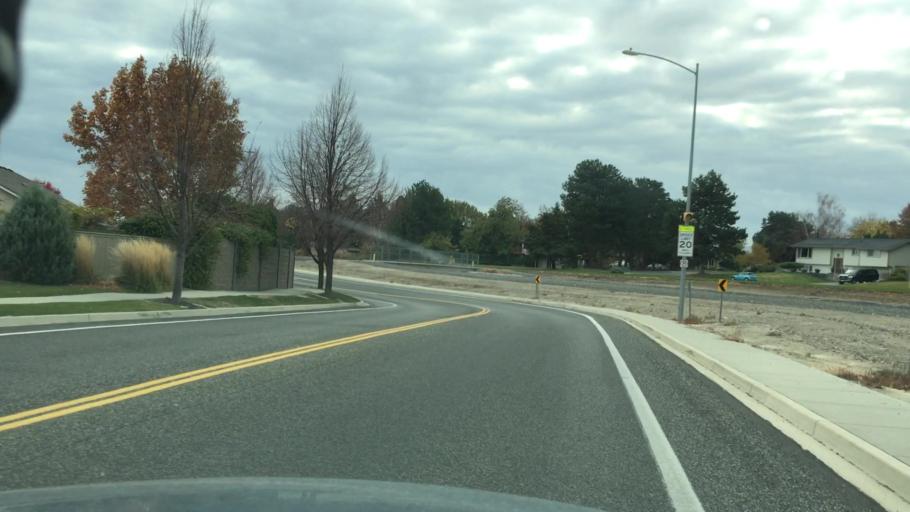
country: US
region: Washington
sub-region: Franklin County
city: West Pasco
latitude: 46.1874
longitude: -119.1912
